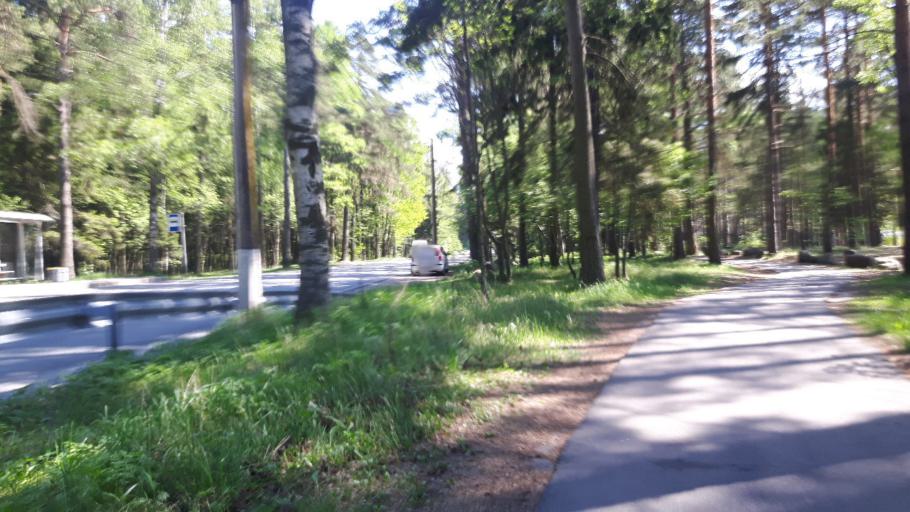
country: RU
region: St.-Petersburg
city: Komarovo
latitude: 60.1720
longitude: 29.8096
